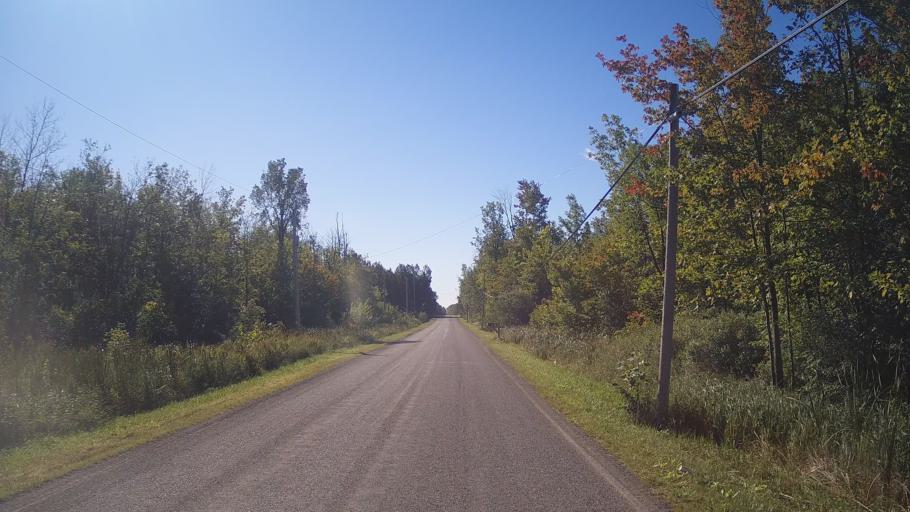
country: CA
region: Ontario
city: Prescott
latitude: 44.9923
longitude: -75.5896
